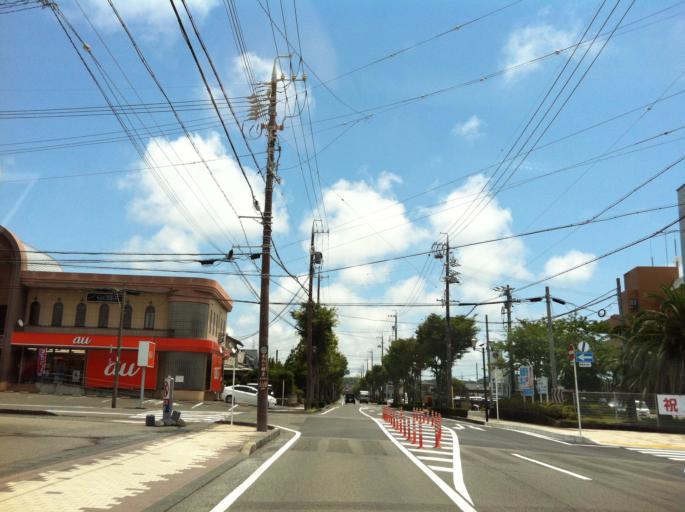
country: JP
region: Shizuoka
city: Sagara
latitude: 34.6388
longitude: 138.1270
